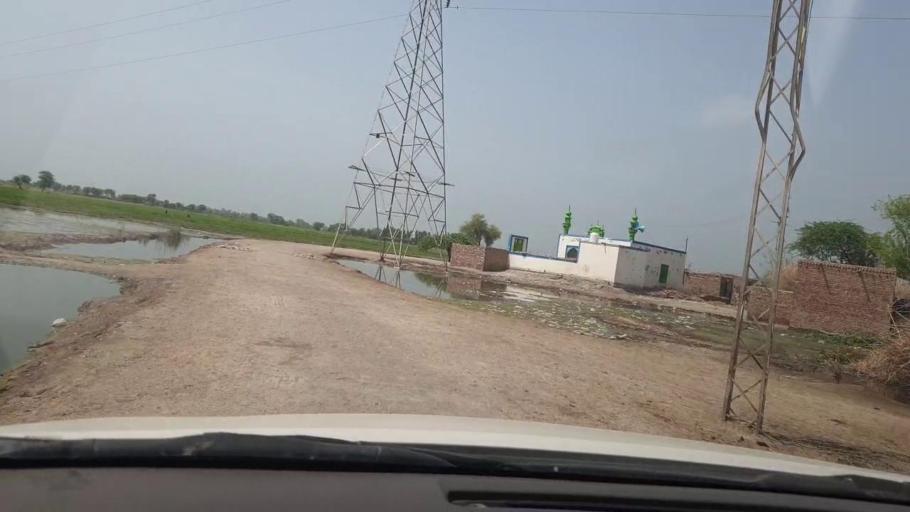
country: PK
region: Sindh
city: Shikarpur
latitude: 27.9985
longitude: 68.6251
